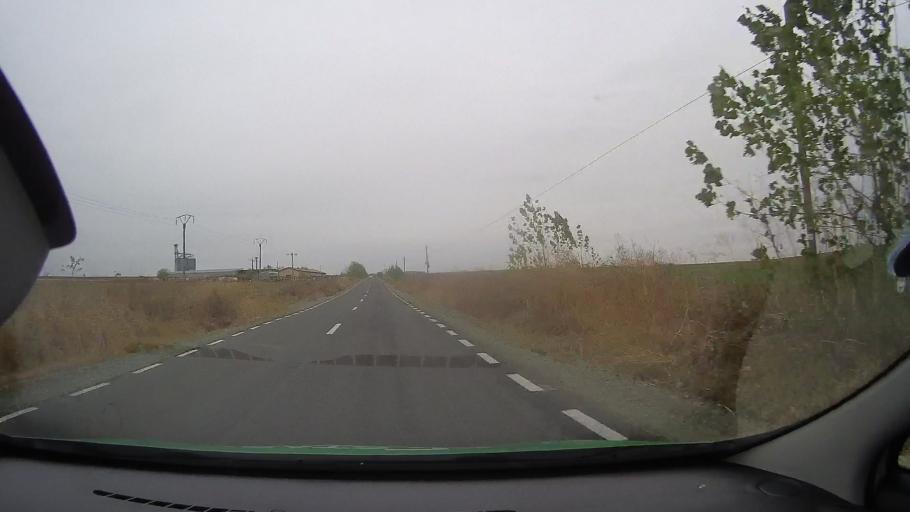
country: RO
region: Constanta
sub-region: Comuna Tortoman
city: Tortoman
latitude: 44.3617
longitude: 28.2099
